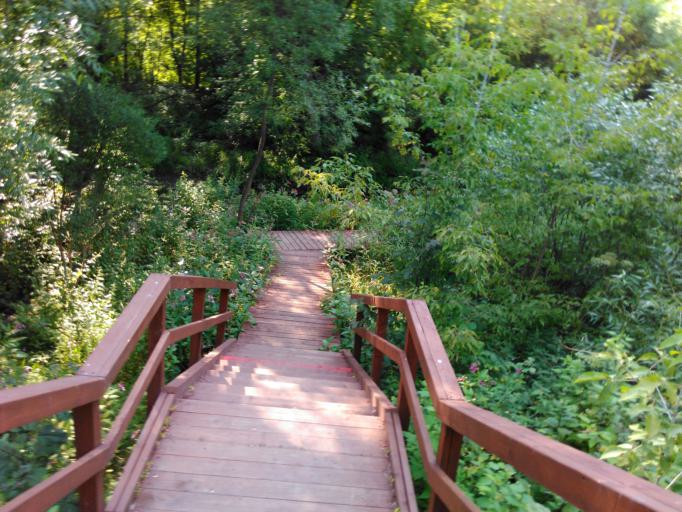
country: RU
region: Moscow
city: Amin'yevo
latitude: 55.7143
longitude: 37.4497
